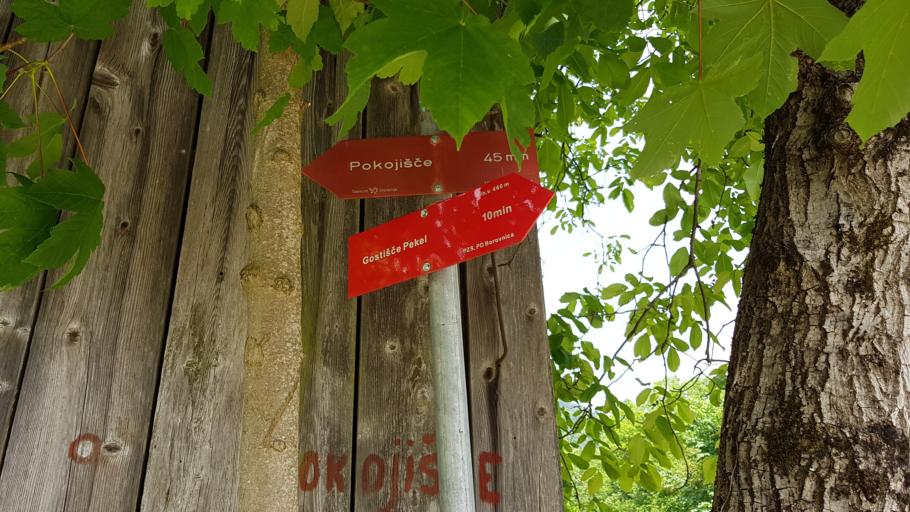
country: SI
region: Borovnica
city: Borovnica
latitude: 45.8937
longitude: 14.3708
